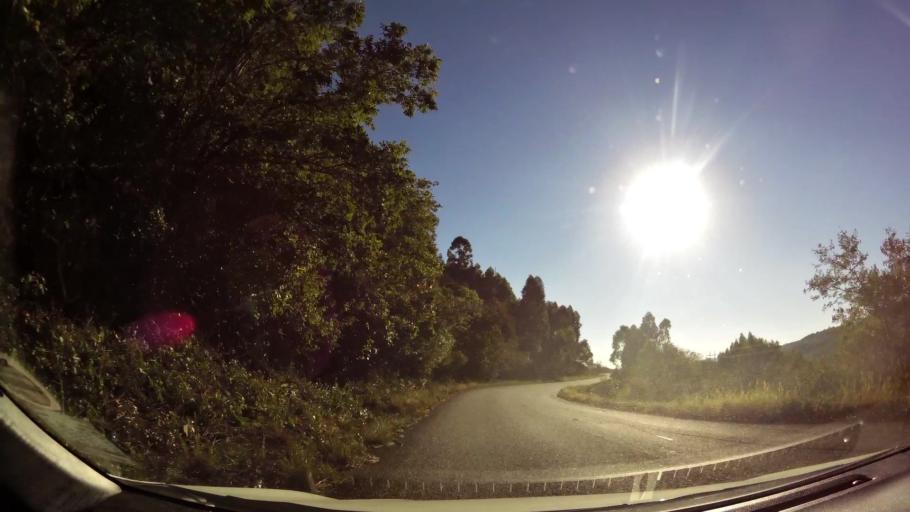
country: ZA
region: Limpopo
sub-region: Mopani District Municipality
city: Tzaneen
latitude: -23.9542
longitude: 30.0112
